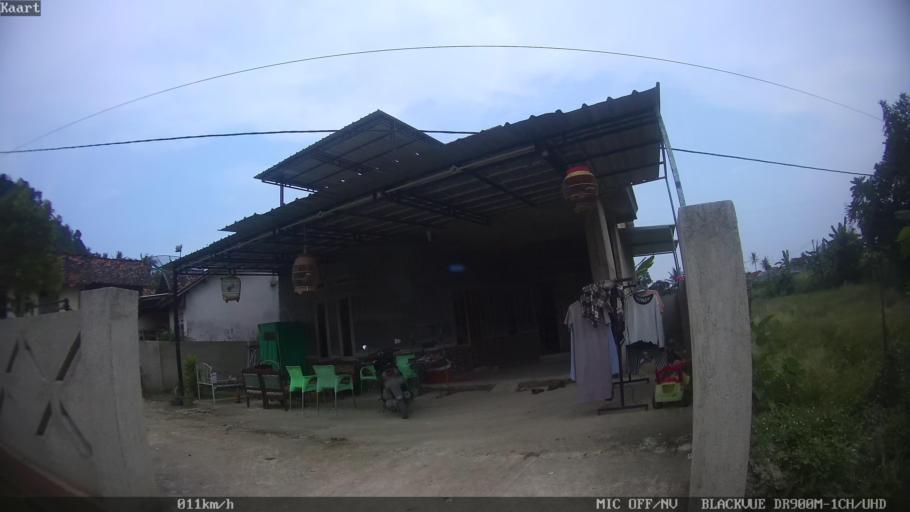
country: ID
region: Lampung
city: Panjang
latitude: -5.4270
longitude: 105.3414
